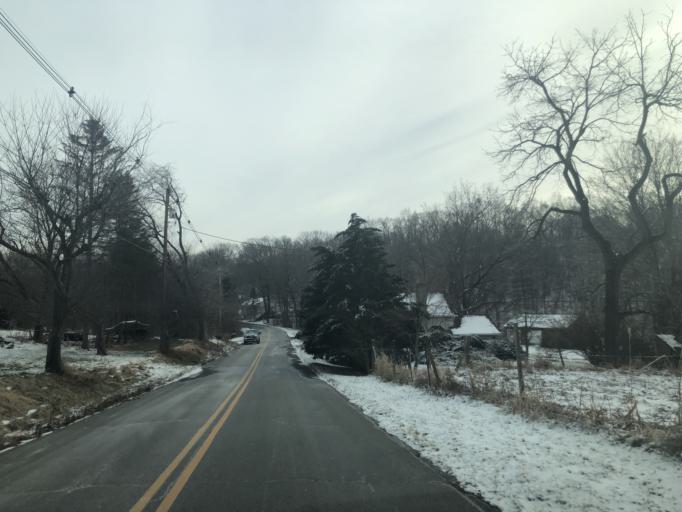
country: US
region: New Jersey
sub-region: Warren County
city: Belvidere
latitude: 40.9308
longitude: -75.0391
